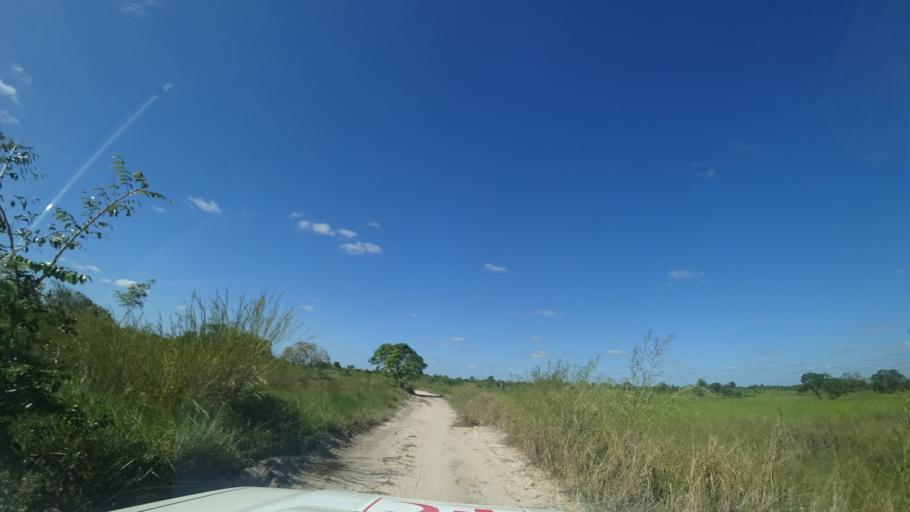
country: MZ
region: Sofala
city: Dondo
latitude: -19.4814
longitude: 34.6245
